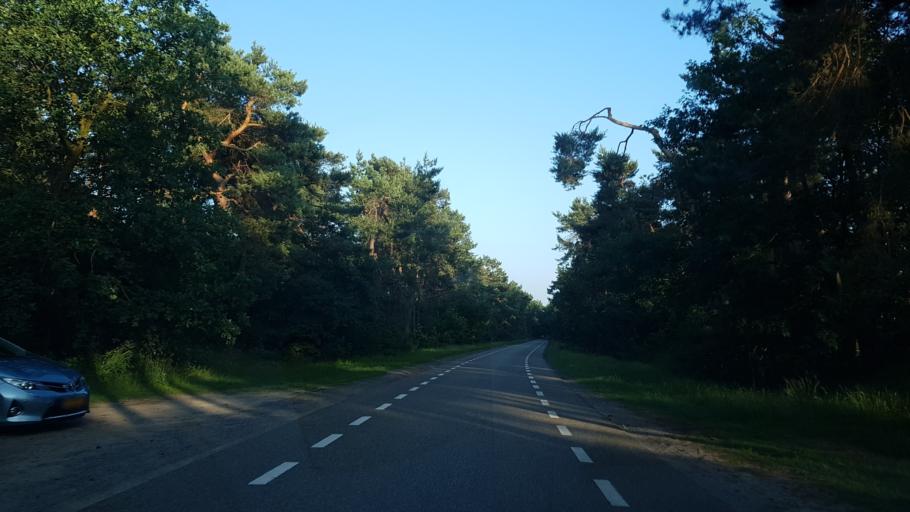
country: NL
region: North Brabant
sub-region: Gemeente Breda
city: Hoge Vucht
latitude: 51.6401
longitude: 4.8085
